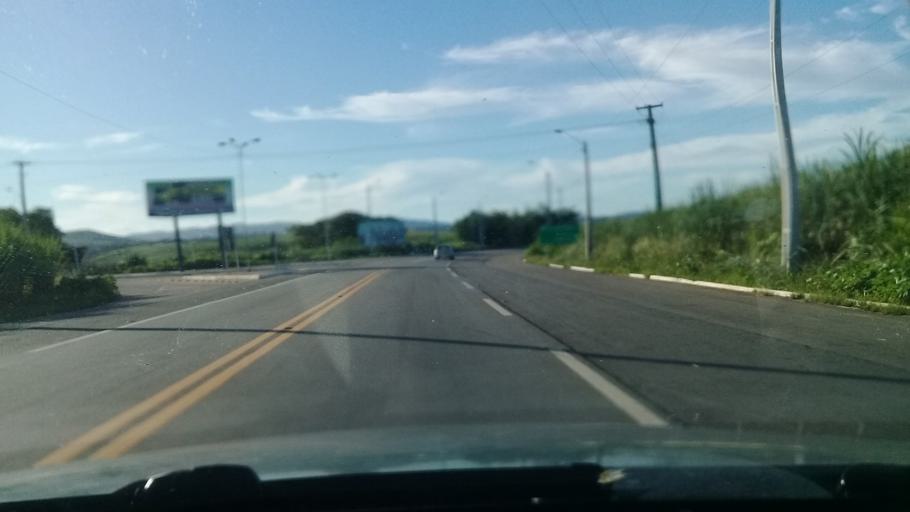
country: BR
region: Pernambuco
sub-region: Nazare Da Mata
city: Nazare da Mata
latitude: -7.7273
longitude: -35.2398
